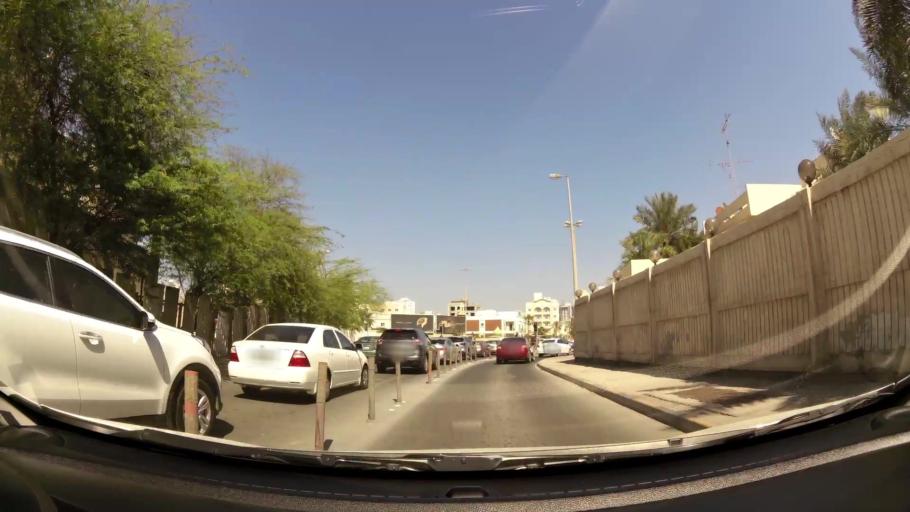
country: BH
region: Manama
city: Manama
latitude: 26.2084
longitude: 50.5973
